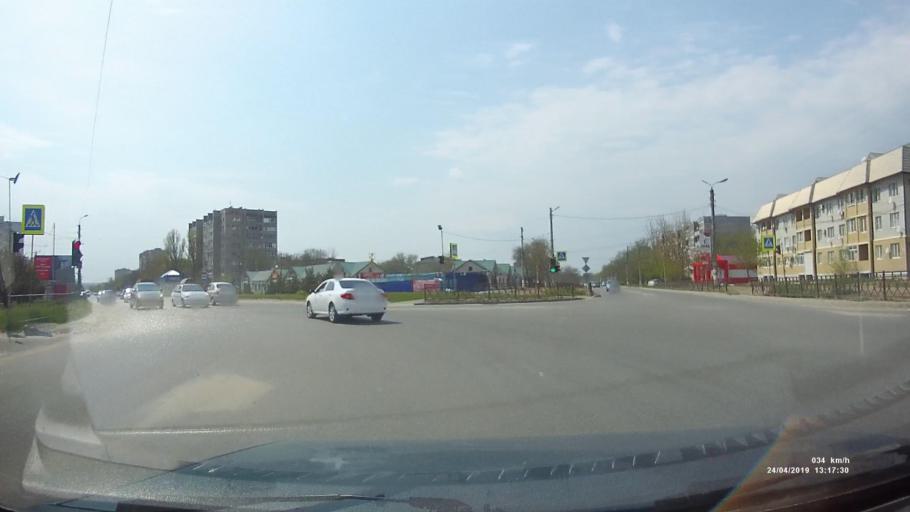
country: RU
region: Kalmykiya
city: Elista
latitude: 46.3055
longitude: 44.2993
